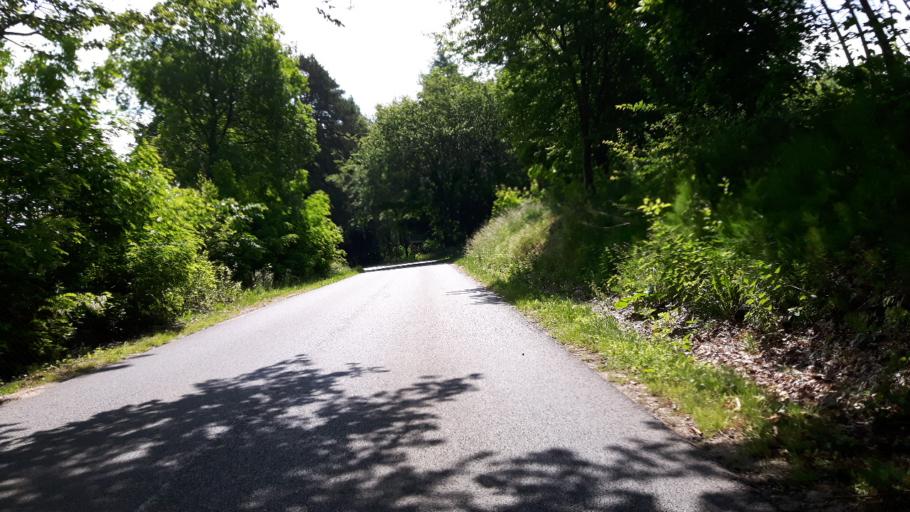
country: PL
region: Pomeranian Voivodeship
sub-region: Powiat wejherowski
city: Choczewo
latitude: 54.7483
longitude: 17.7953
